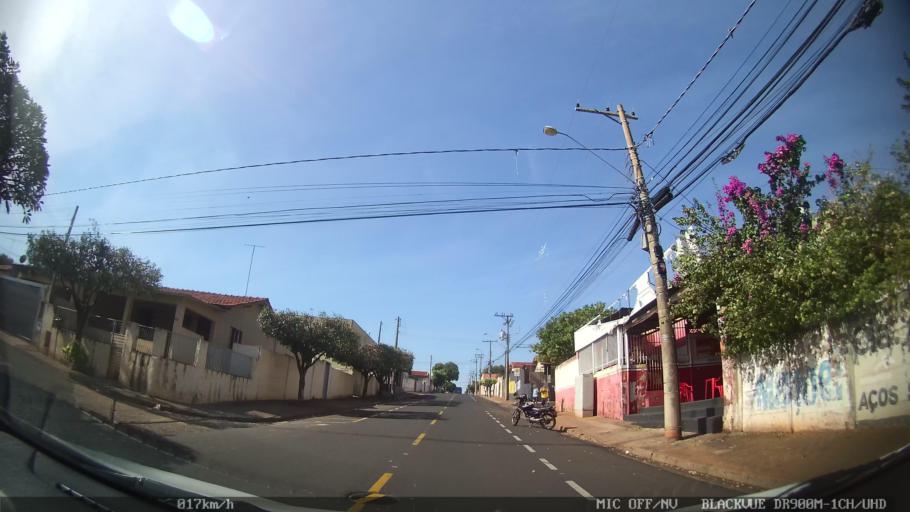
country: BR
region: Sao Paulo
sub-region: Sao Jose Do Rio Preto
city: Sao Jose do Rio Preto
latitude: -20.7946
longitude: -49.4212
